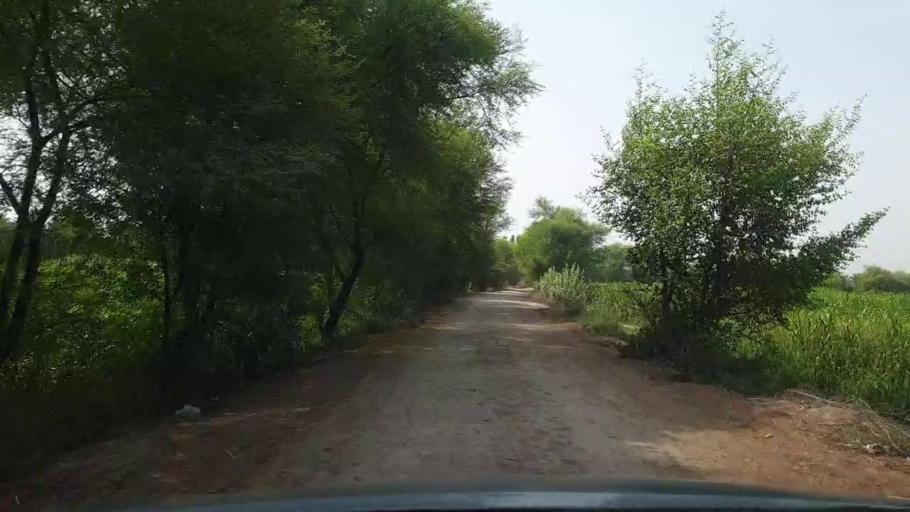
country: PK
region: Sindh
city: Rohri
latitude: 27.6570
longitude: 69.0118
